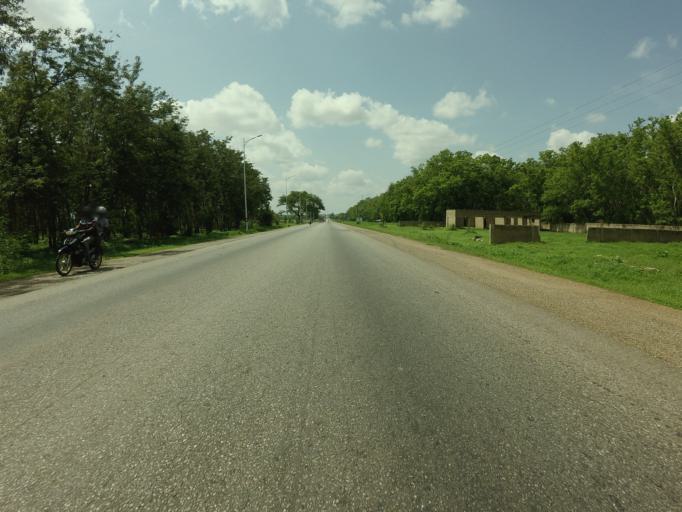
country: GH
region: Northern
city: Savelugu
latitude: 9.5380
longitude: -0.8394
